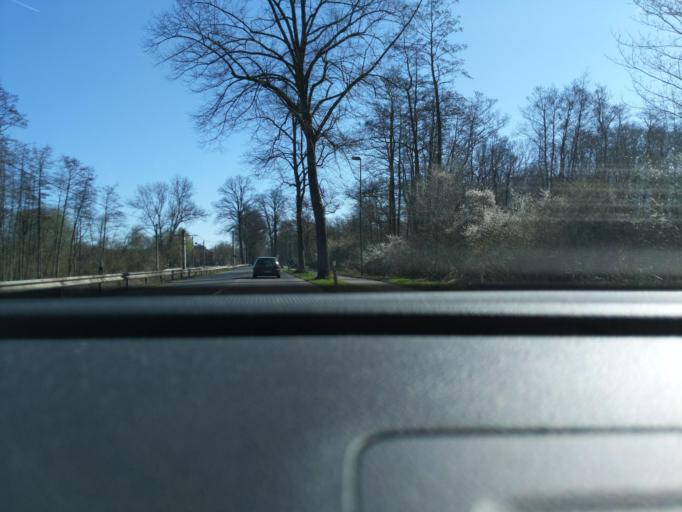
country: DE
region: North Rhine-Westphalia
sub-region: Regierungsbezirk Dusseldorf
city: Meerbusch
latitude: 51.2661
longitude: 6.6619
